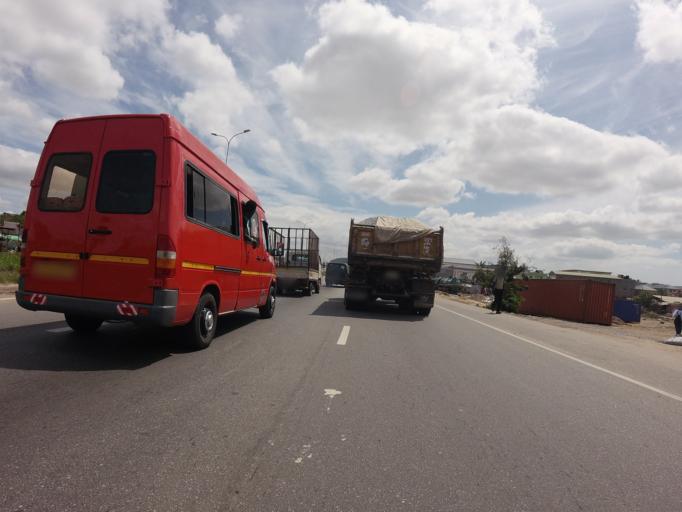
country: GH
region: Central
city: Kasoa
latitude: 5.5359
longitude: -0.4091
